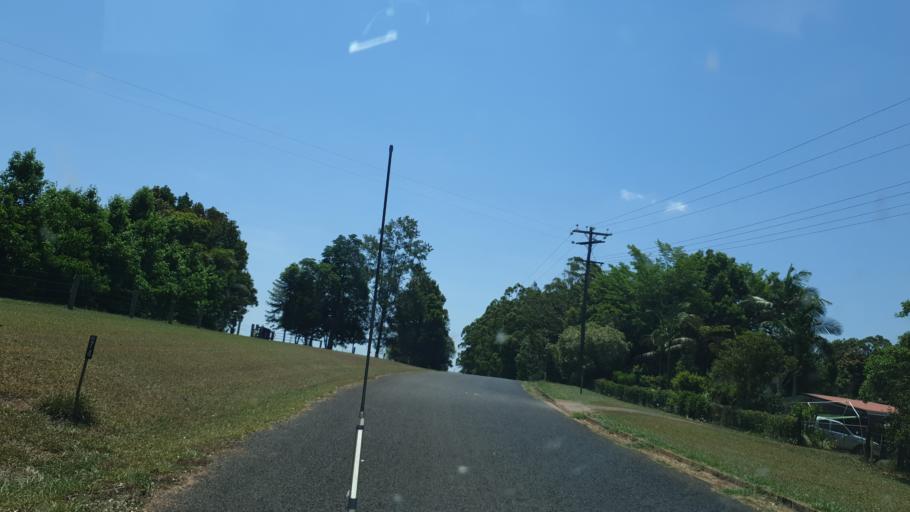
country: AU
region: Queensland
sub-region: Tablelands
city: Atherton
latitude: -17.3492
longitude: 145.6165
